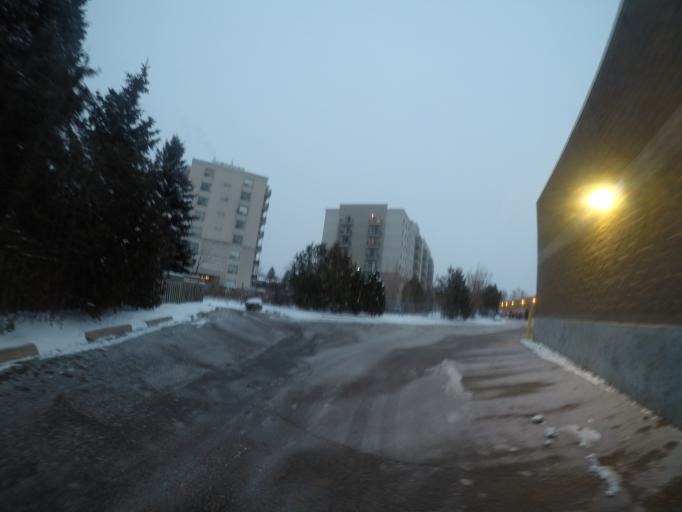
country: CA
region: Ontario
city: Waterloo
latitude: 43.4896
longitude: -80.4914
